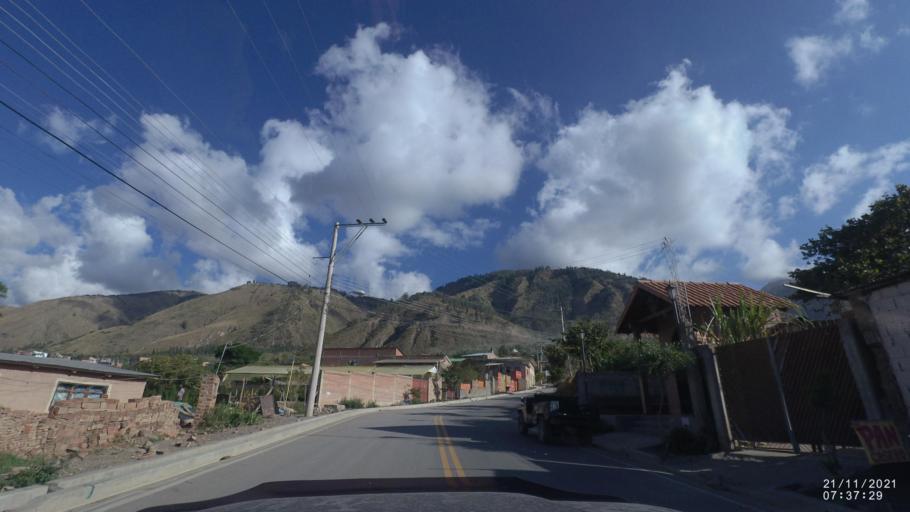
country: BO
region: Cochabamba
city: Cochabamba
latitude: -17.3249
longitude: -66.2176
